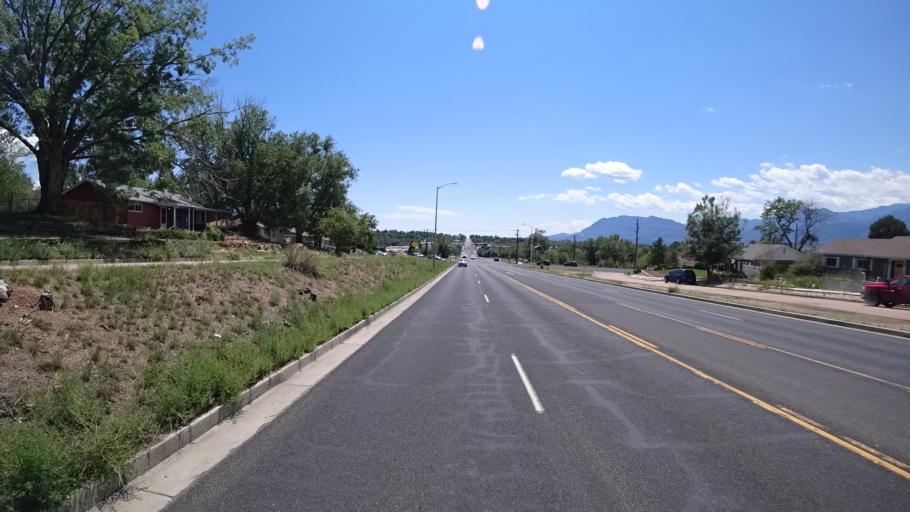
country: US
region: Colorado
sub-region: El Paso County
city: Colorado Springs
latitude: 38.8631
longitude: -104.7941
